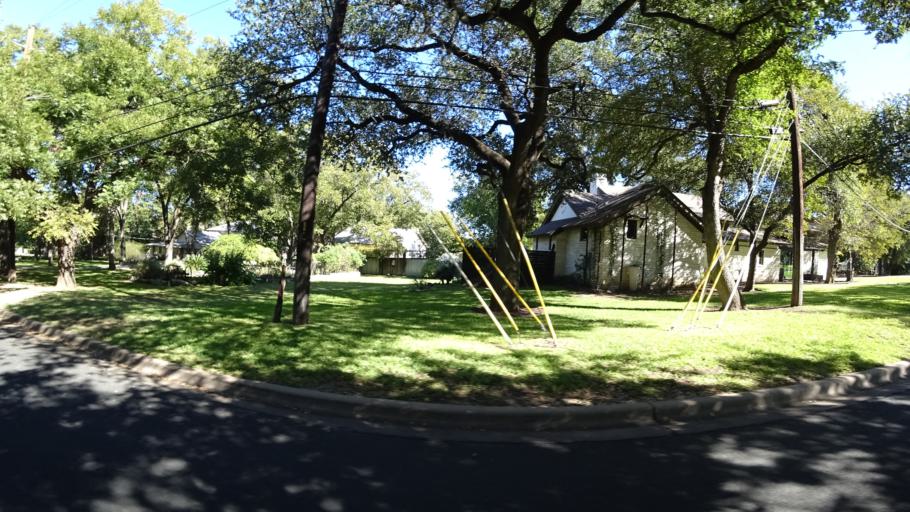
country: US
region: Texas
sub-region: Travis County
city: Rollingwood
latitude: 30.2453
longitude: -97.7742
